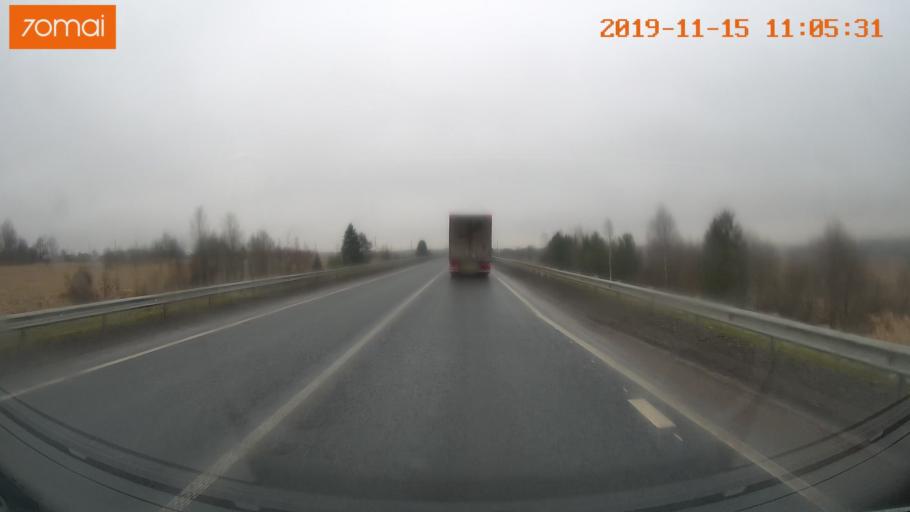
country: RU
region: Vologda
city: Chebsara
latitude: 59.1185
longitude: 39.0060
